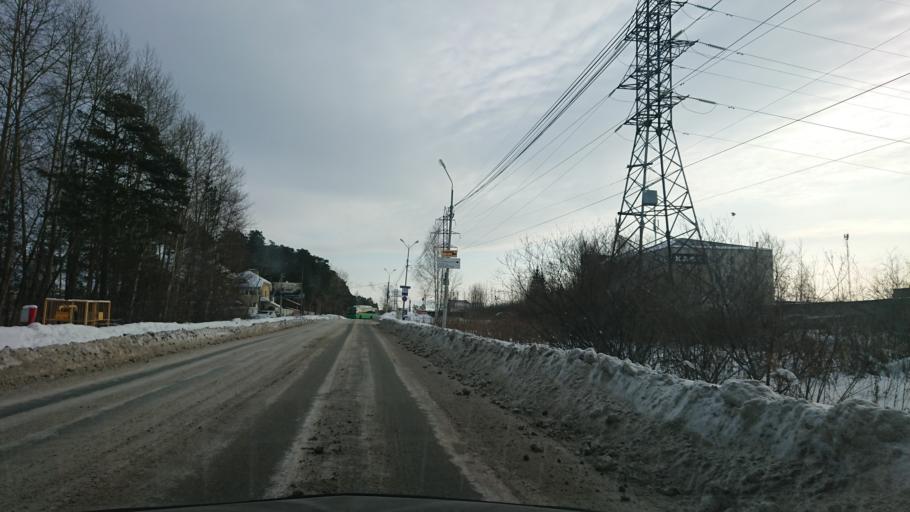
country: RU
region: Sverdlovsk
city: Sovkhoznyy
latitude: 56.7794
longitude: 60.5615
